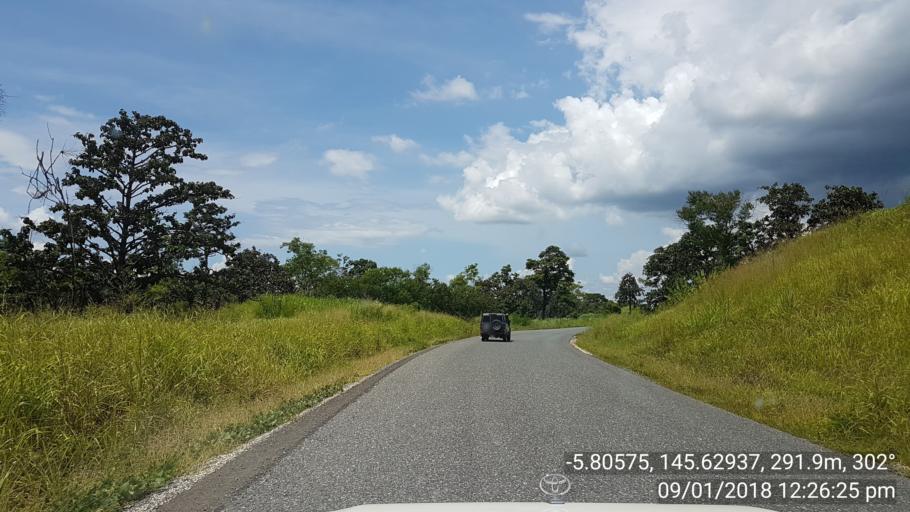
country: PG
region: Eastern Highlands
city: Goroka
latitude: -5.8059
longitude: 145.6296
